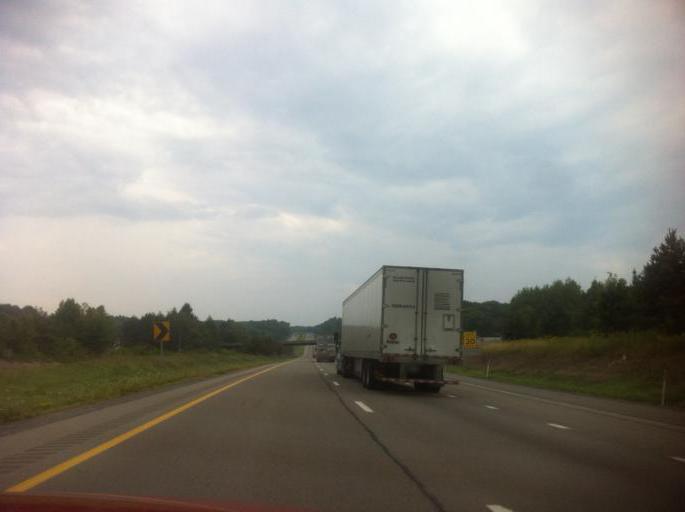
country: US
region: Pennsylvania
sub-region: Jefferson County
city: Brookville
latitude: 41.1858
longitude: -79.1945
